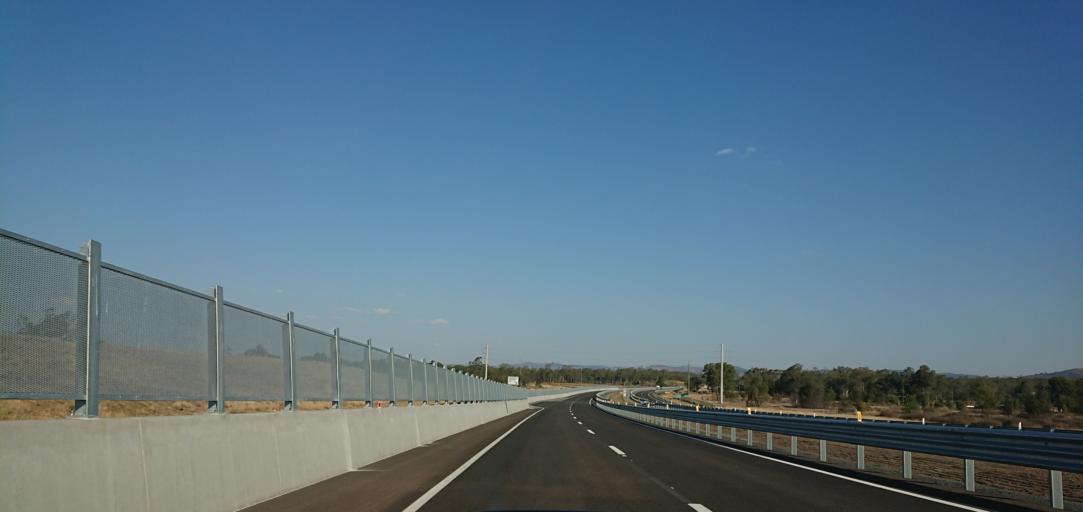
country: AU
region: Queensland
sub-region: Toowoomba
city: East Toowoomba
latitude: -27.5284
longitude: 152.0716
